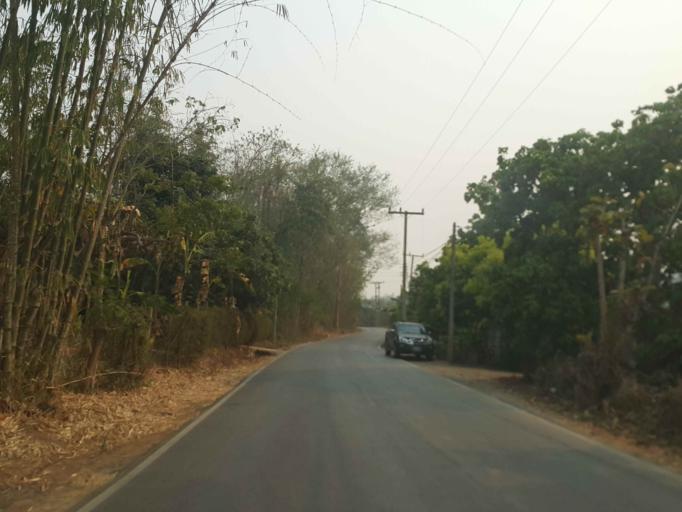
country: TH
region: Chiang Mai
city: Mae Taeng
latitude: 19.1064
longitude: 98.8989
